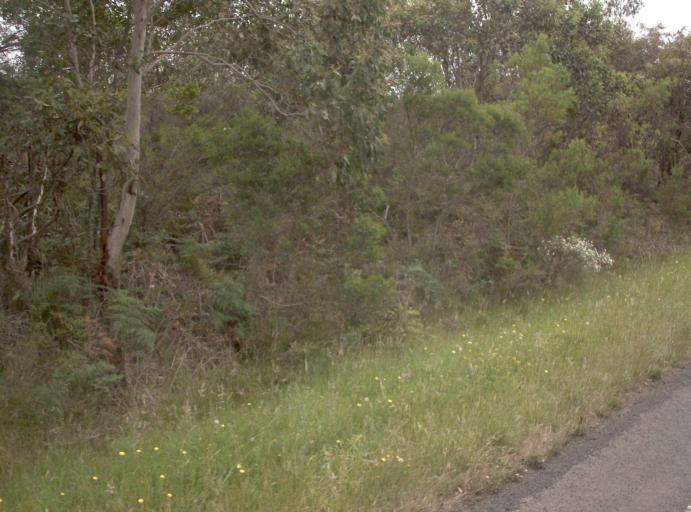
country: AU
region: Victoria
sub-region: Bass Coast
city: North Wonthaggi
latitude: -38.5738
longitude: 145.9778
